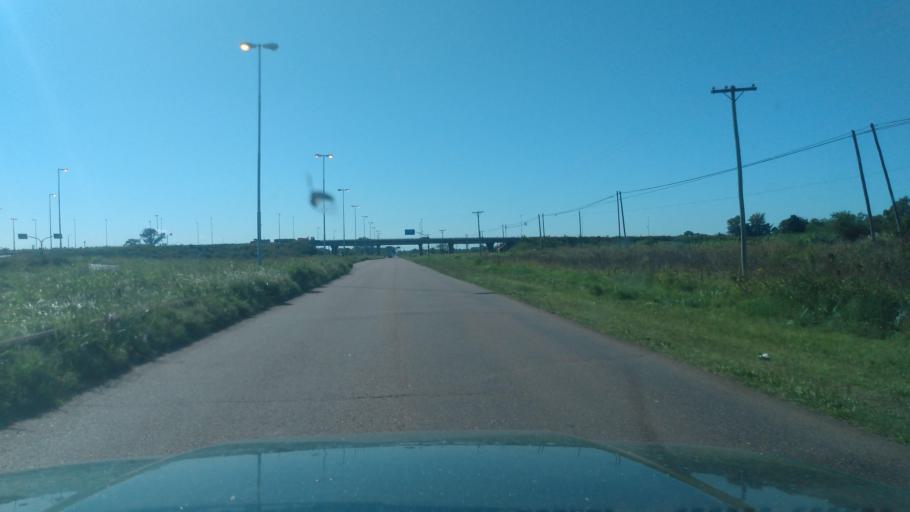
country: AR
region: Buenos Aires
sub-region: Partido de Lujan
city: Lujan
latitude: -34.5879
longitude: -59.0412
